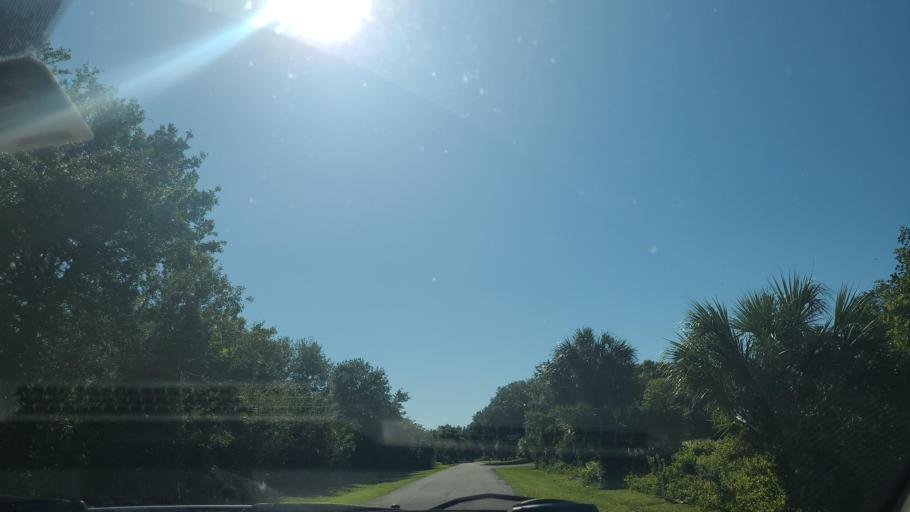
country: US
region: Florida
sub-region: Indian River County
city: Sebastian
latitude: 27.7561
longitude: -80.4835
